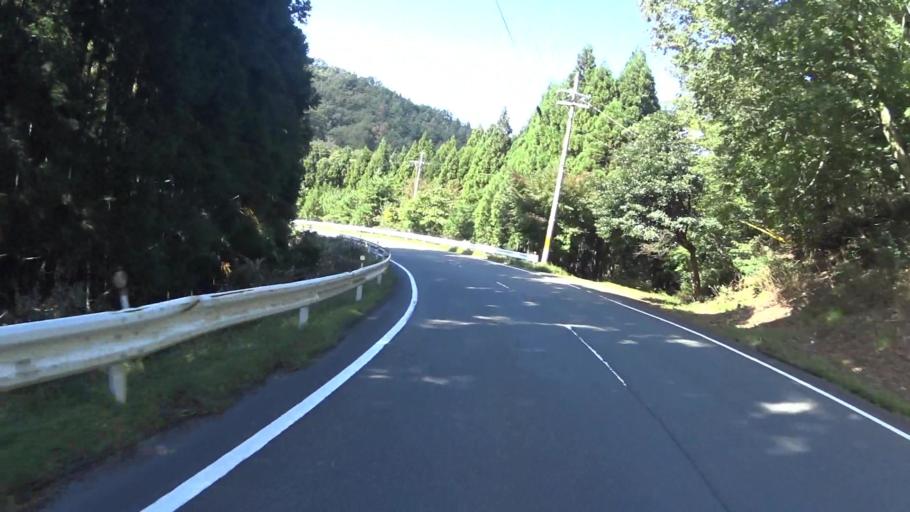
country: JP
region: Hyogo
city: Toyooka
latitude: 35.5363
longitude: 134.9787
